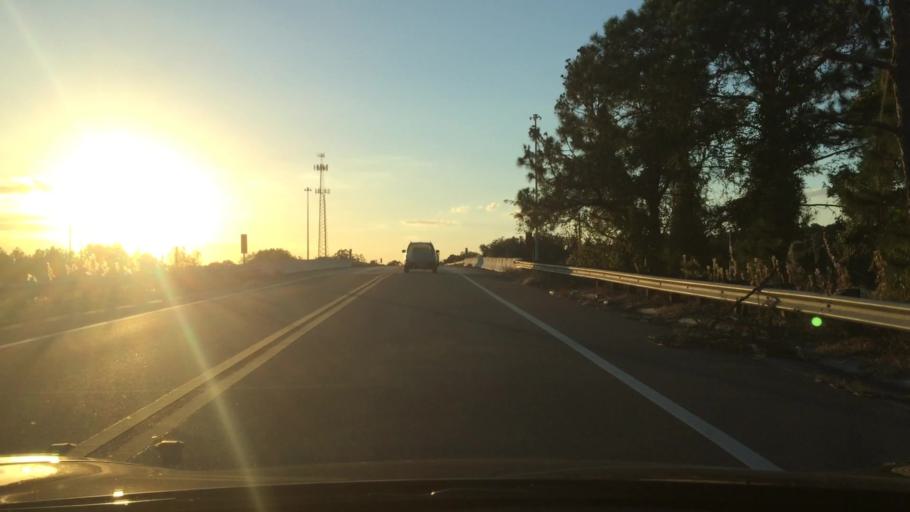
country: US
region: Florida
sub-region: Hillsborough County
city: Pebble Creek
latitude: 28.1713
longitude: -82.3917
